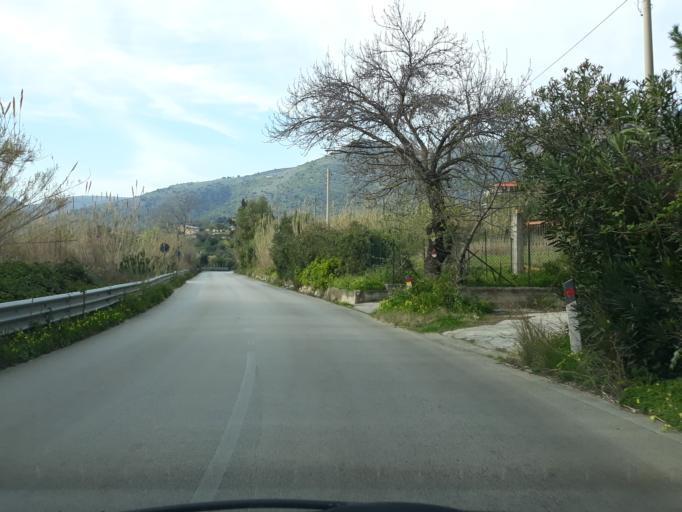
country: IT
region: Sicily
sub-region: Palermo
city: Giardinello
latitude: 38.0720
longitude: 13.1542
